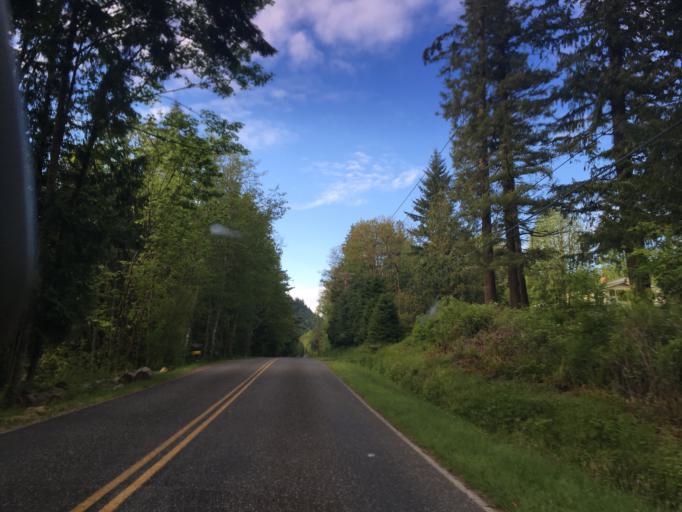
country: US
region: Washington
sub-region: Whatcom County
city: Sudden Valley
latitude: 48.7692
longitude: -122.3553
